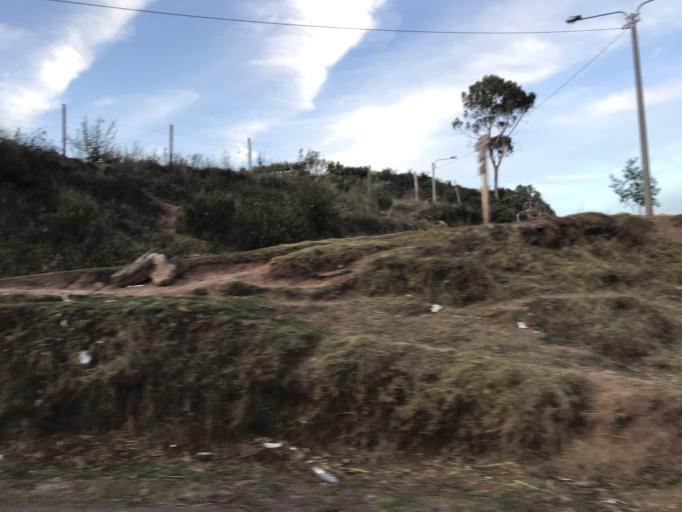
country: PE
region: Cusco
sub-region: Provincia de Cusco
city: Cusco
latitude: -13.5076
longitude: -71.9701
